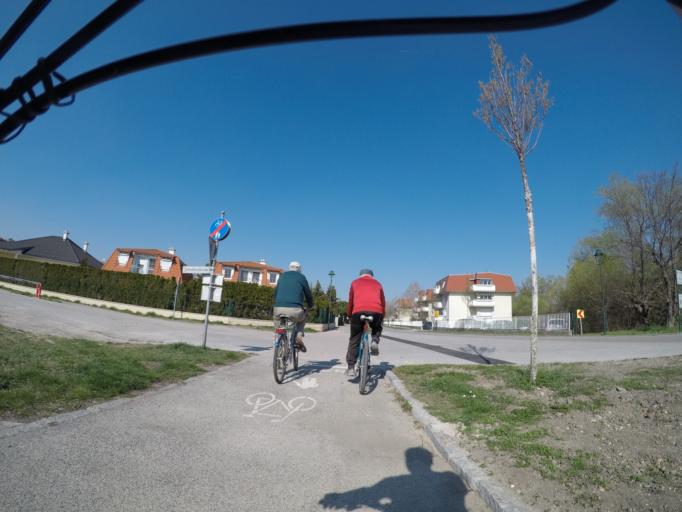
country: AT
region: Lower Austria
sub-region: Politischer Bezirk Modling
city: Laxenburg
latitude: 48.0630
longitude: 16.3499
